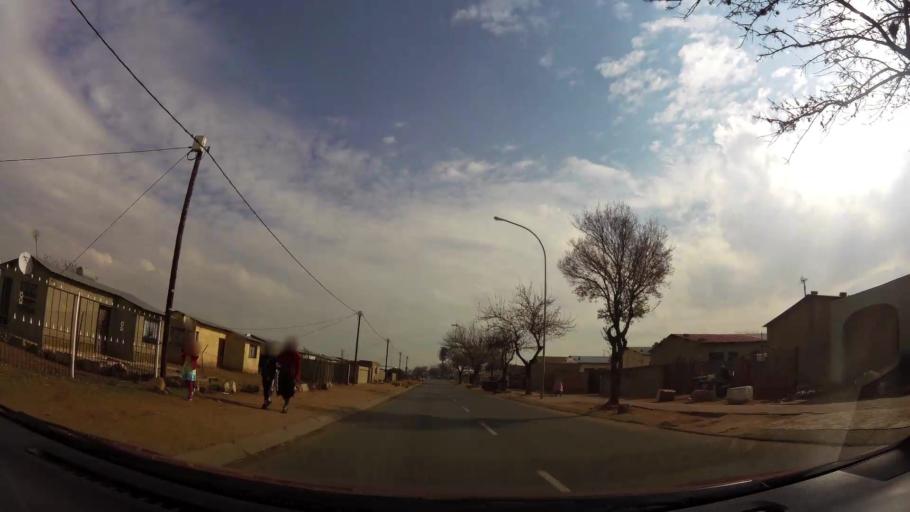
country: ZA
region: Gauteng
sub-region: City of Johannesburg Metropolitan Municipality
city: Soweto
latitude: -26.2589
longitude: 27.8192
